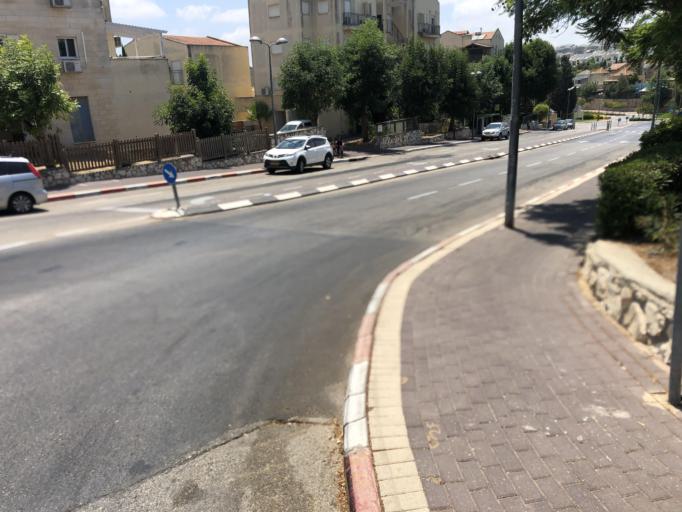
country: IL
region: Haifa
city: Daliyat el Karmil
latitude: 32.6374
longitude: 35.0867
